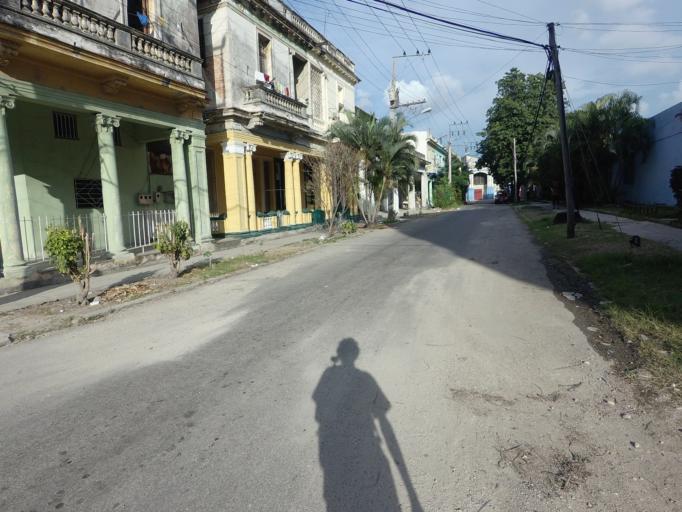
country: CU
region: La Habana
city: Havana
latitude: 23.1274
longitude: -82.3803
